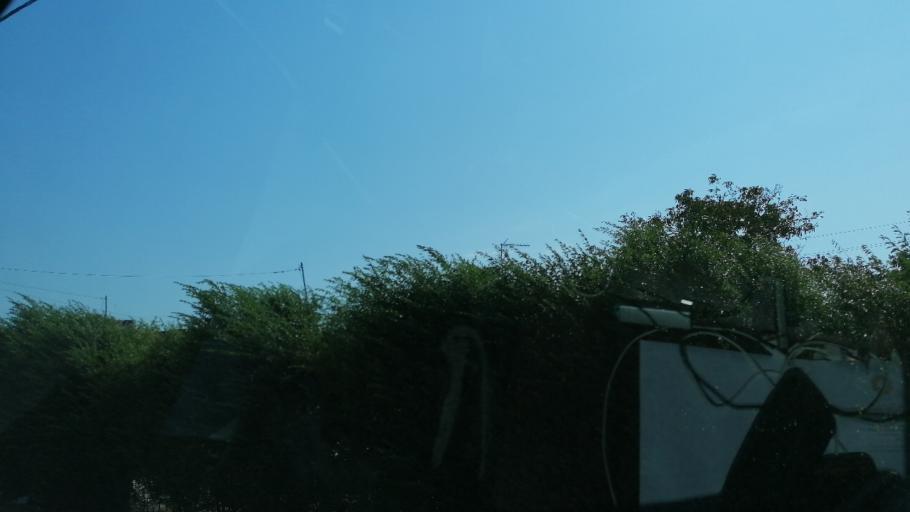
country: PT
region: Santarem
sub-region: Benavente
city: Poceirao
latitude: 38.7418
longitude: -8.6591
